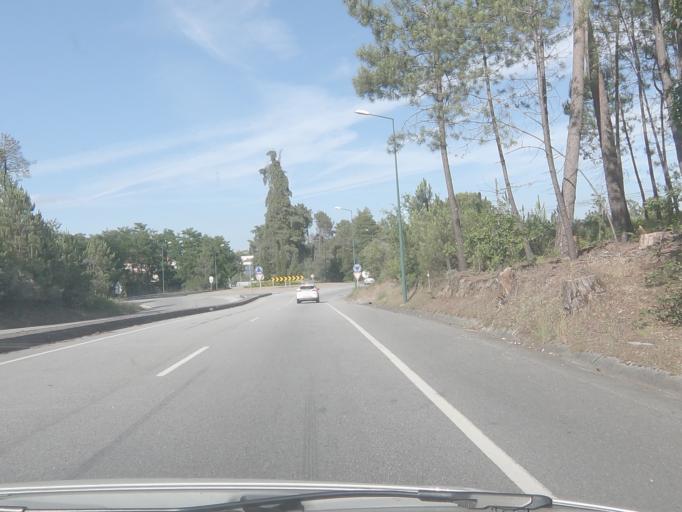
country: PT
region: Viseu
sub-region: Viseu
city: Viseu
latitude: 40.6296
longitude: -7.9372
